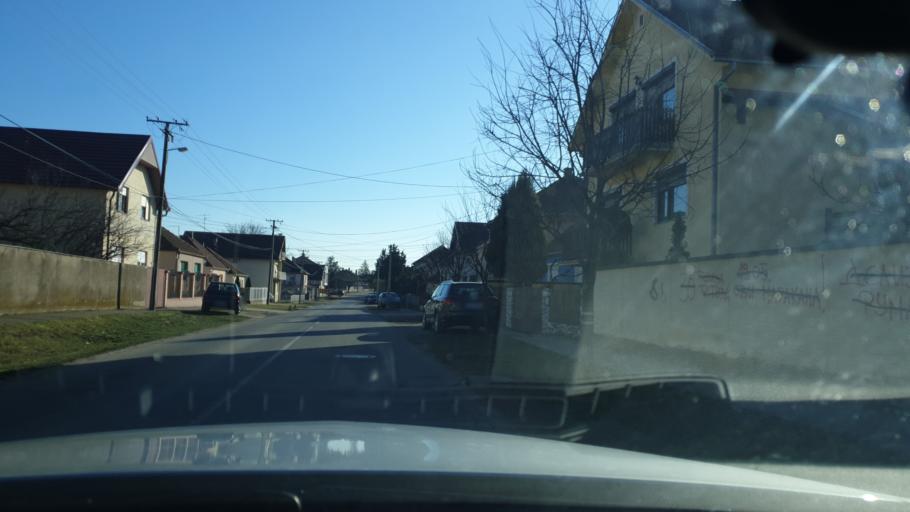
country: RS
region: Autonomna Pokrajina Vojvodina
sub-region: Sremski Okrug
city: Ruma
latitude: 45.0150
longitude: 19.8166
